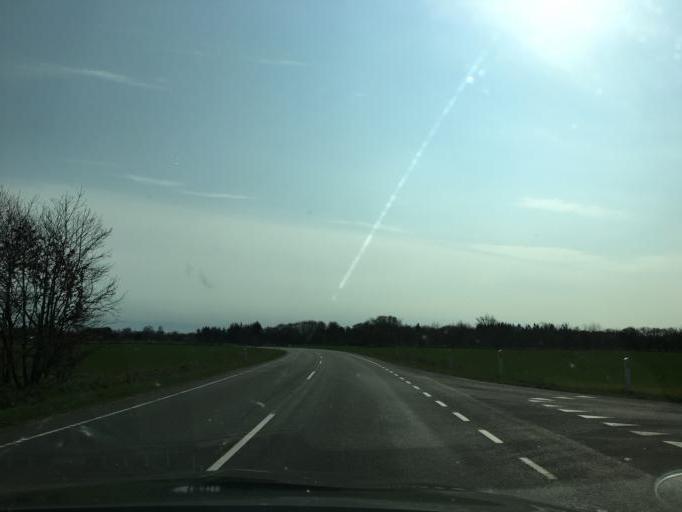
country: DK
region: South Denmark
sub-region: Vejen Kommune
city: Vejen
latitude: 55.4696
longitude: 9.1746
